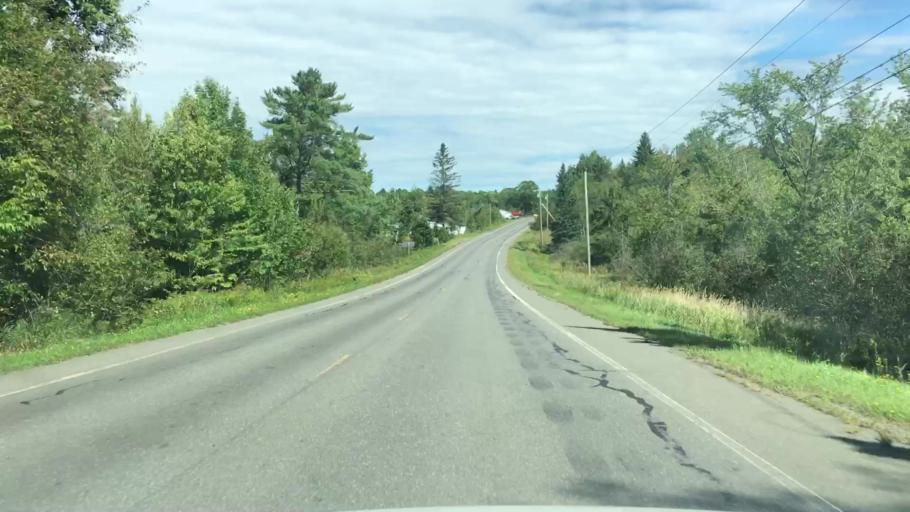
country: US
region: Maine
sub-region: Penobscot County
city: Garland
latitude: 45.0794
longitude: -69.2303
